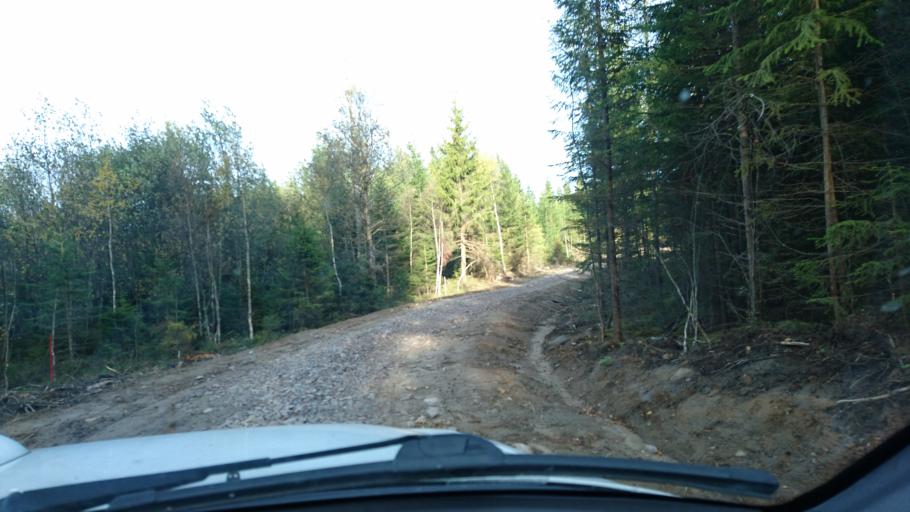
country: SE
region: Vaestra Goetaland
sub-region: Ulricehamns Kommun
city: Ulricehamn
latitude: 57.9383
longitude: 13.5509
